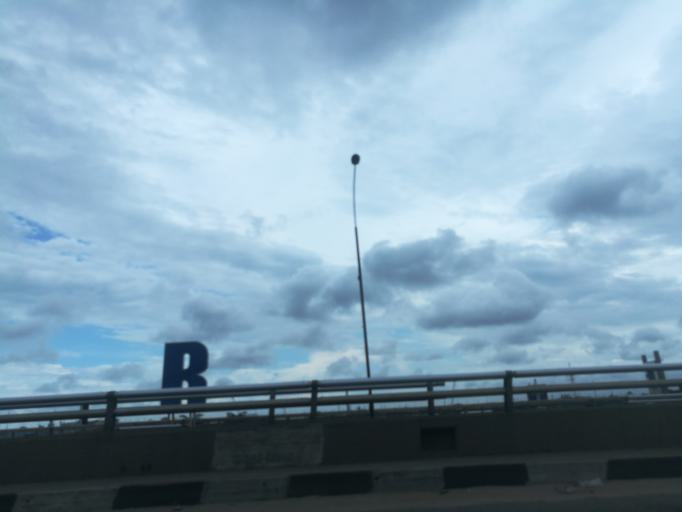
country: NG
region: Lagos
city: Lagos
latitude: 6.4665
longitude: 3.3852
